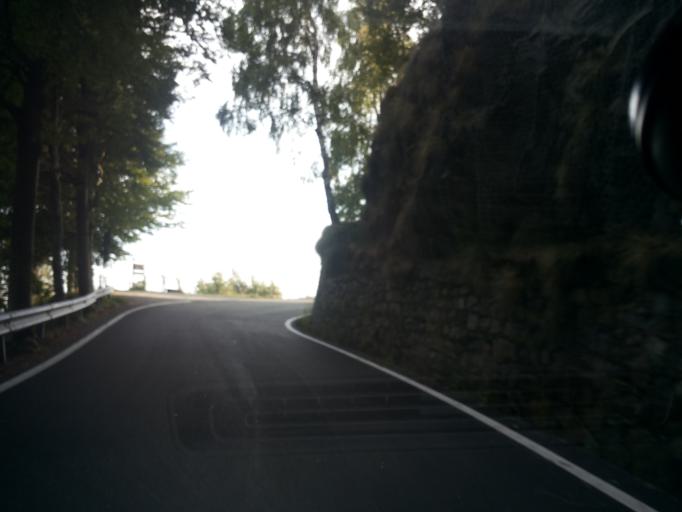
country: IT
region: Piedmont
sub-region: Provincia di Biella
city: Mosso
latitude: 45.6686
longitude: 8.1337
